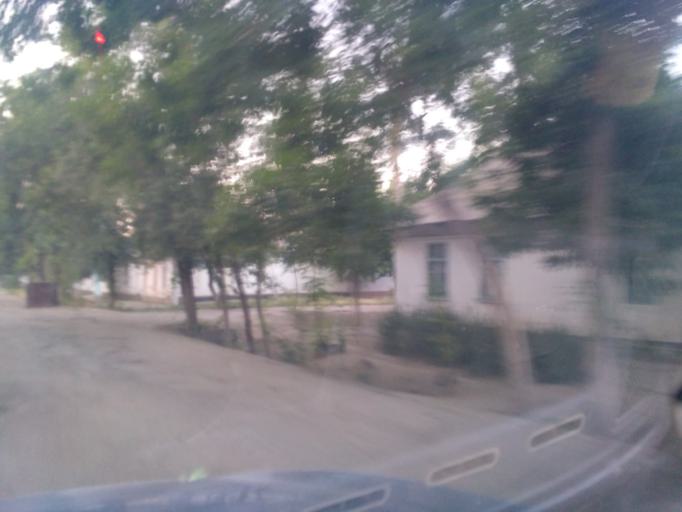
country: UZ
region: Sirdaryo
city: Guliston
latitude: 40.5017
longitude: 68.7694
